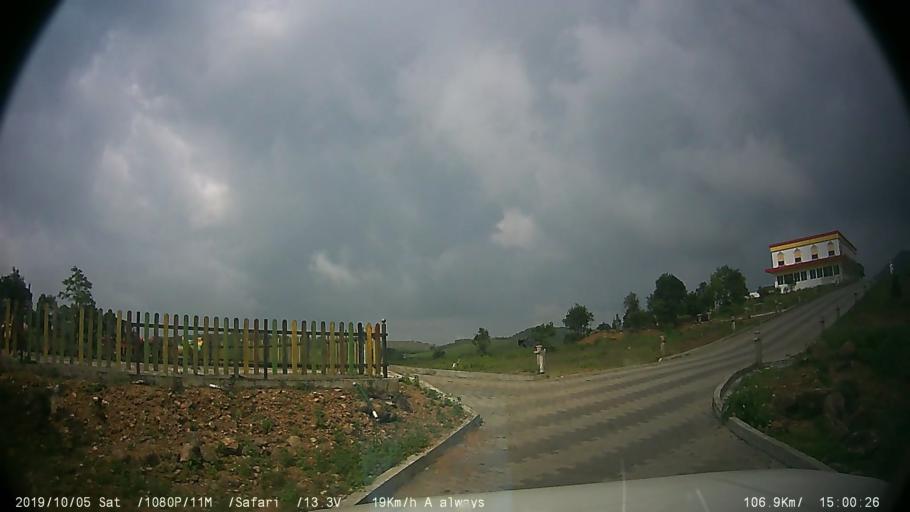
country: IN
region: Kerala
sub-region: Kottayam
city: Erattupetta
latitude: 9.6210
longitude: 76.9325
